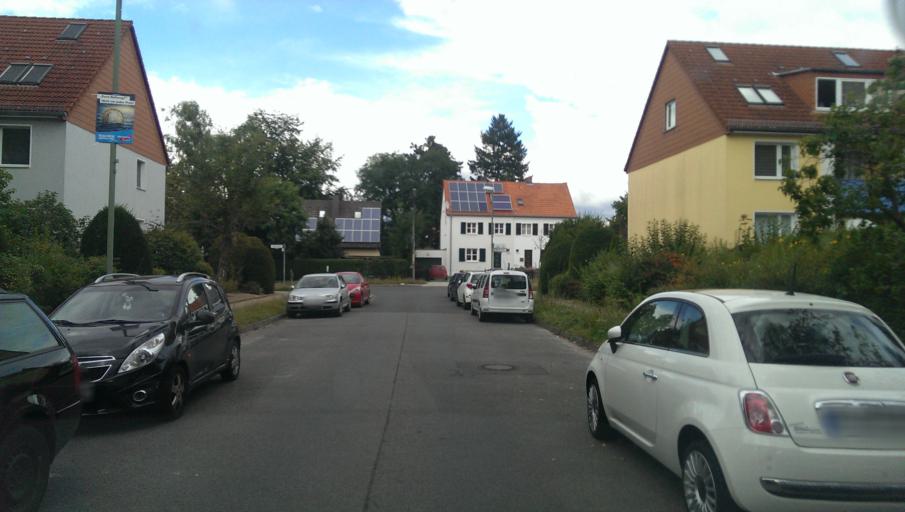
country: DE
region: Brandenburg
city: Teltow
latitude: 52.4125
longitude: 13.2606
